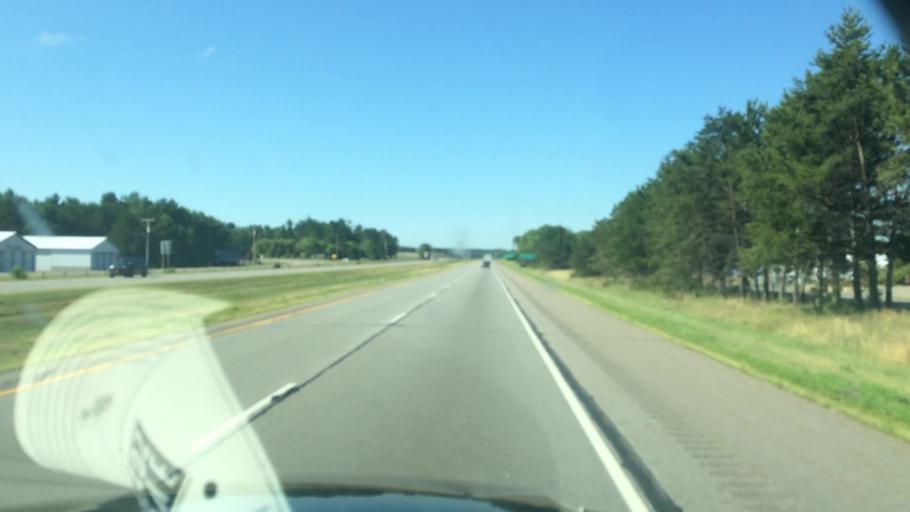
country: US
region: Wisconsin
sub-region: Marathon County
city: Evergreen
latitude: 44.8199
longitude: -89.6659
